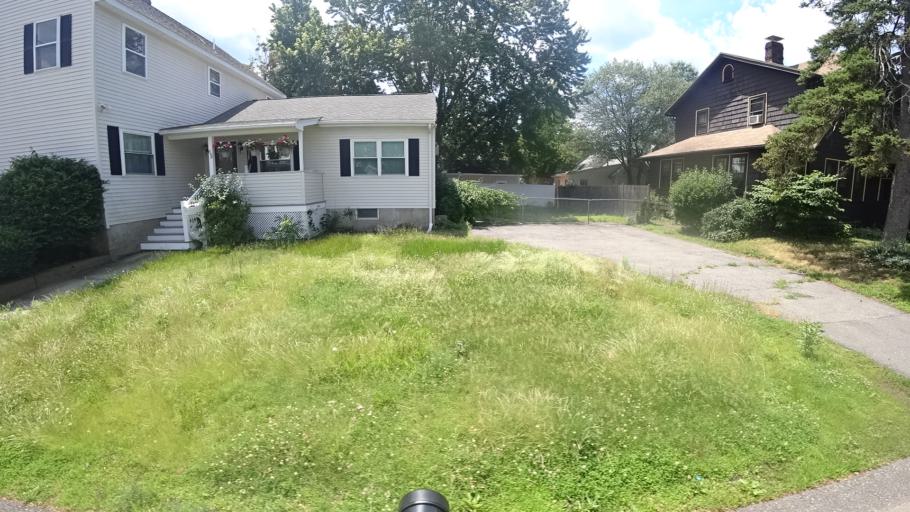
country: US
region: Massachusetts
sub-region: Norfolk County
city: Dedham
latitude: 42.2731
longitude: -71.1792
